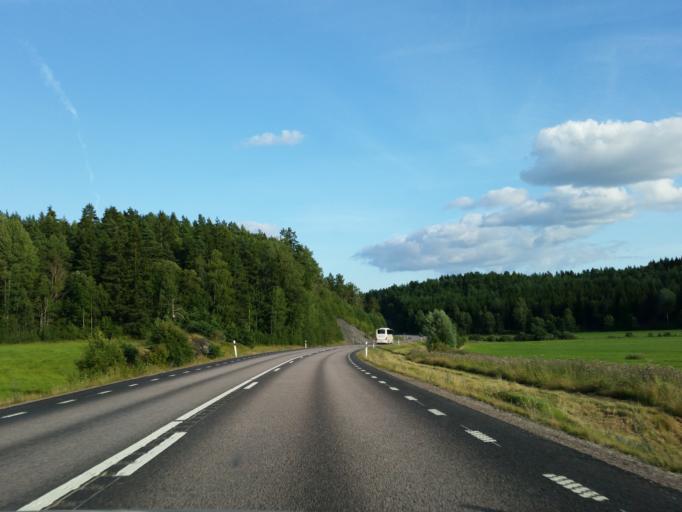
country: SE
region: Soedermanland
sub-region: Gnesta Kommun
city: Gnesta
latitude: 59.0391
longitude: 17.2966
